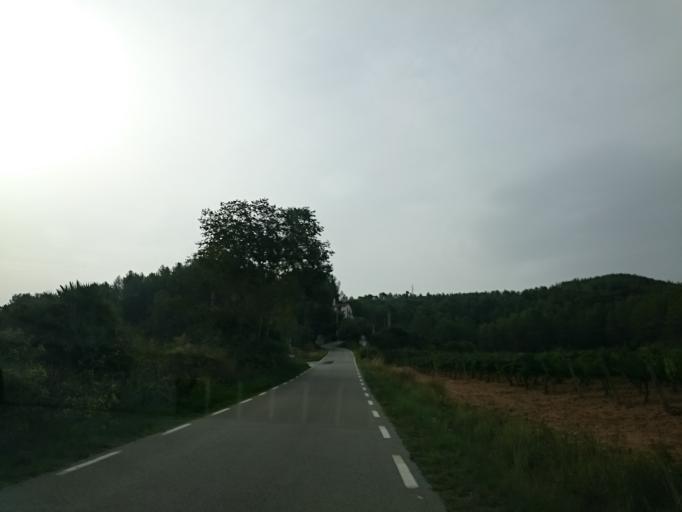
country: ES
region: Catalonia
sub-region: Provincia de Barcelona
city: Olivella
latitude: 41.3118
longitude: 1.8078
